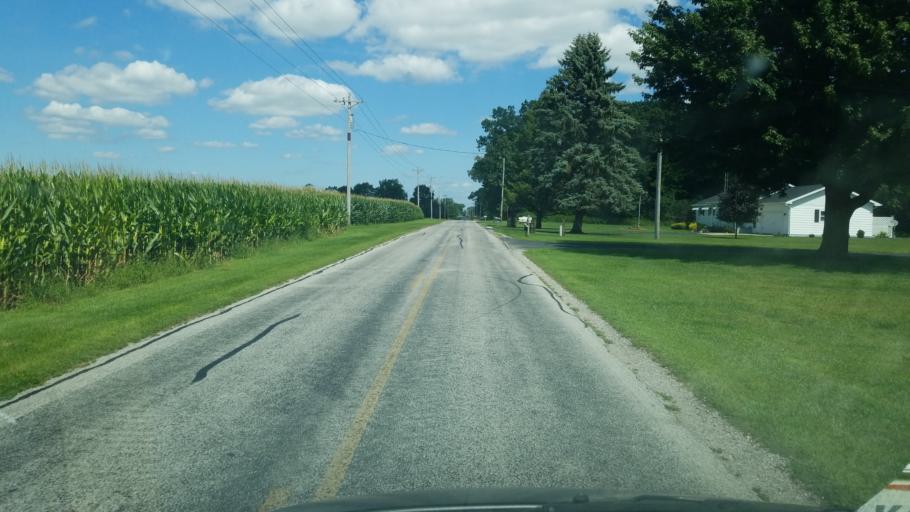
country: US
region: Ohio
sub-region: Fulton County
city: Swanton
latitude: 41.5467
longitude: -83.9408
